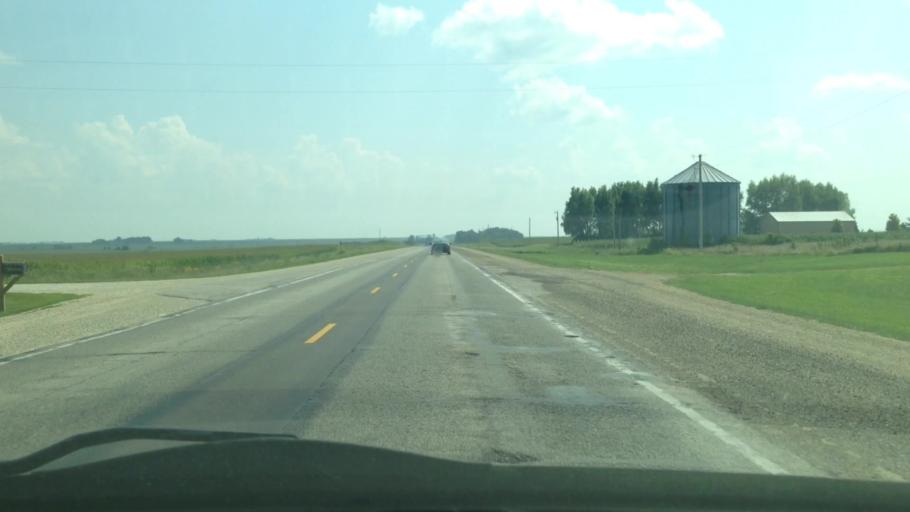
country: US
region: Iowa
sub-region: Howard County
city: Cresco
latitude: 43.3546
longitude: -92.2985
